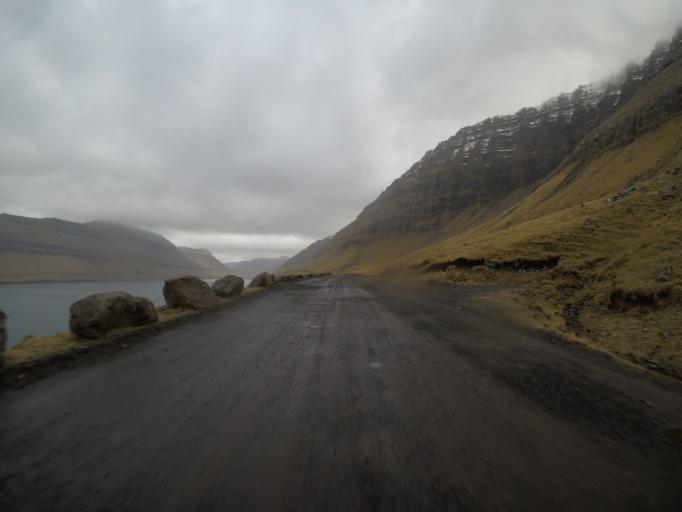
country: FO
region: Nordoyar
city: Klaksvik
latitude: 62.3378
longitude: -6.5787
